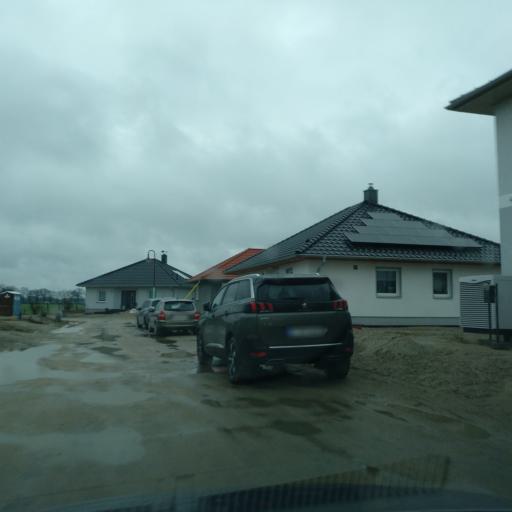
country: DE
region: Brandenburg
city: Neuenhagen
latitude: 52.5033
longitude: 13.6929
